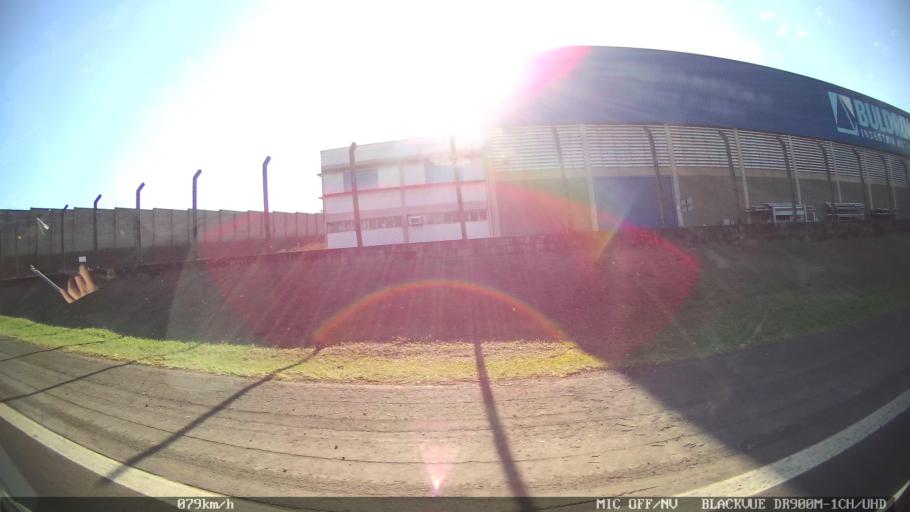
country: BR
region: Sao Paulo
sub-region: Piracicaba
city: Piracicaba
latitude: -22.6754
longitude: -47.6322
